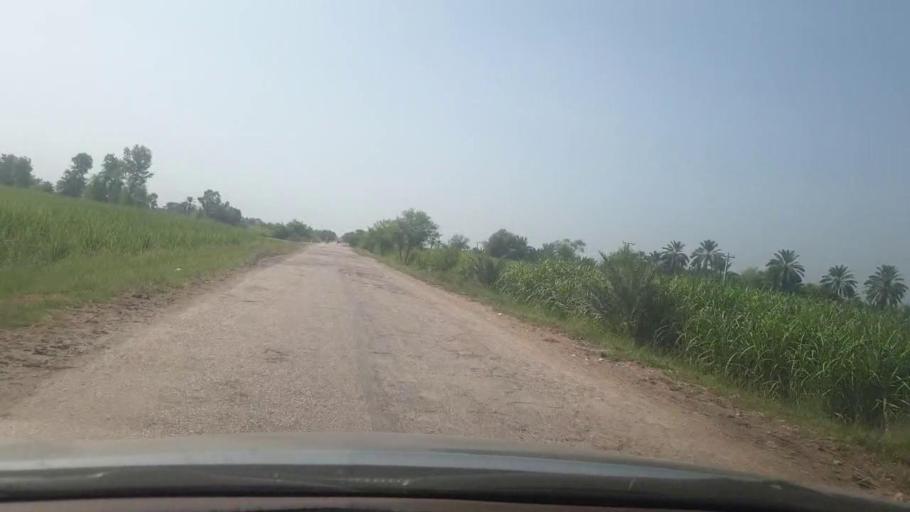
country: PK
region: Sindh
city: Gambat
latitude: 27.3097
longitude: 68.5631
